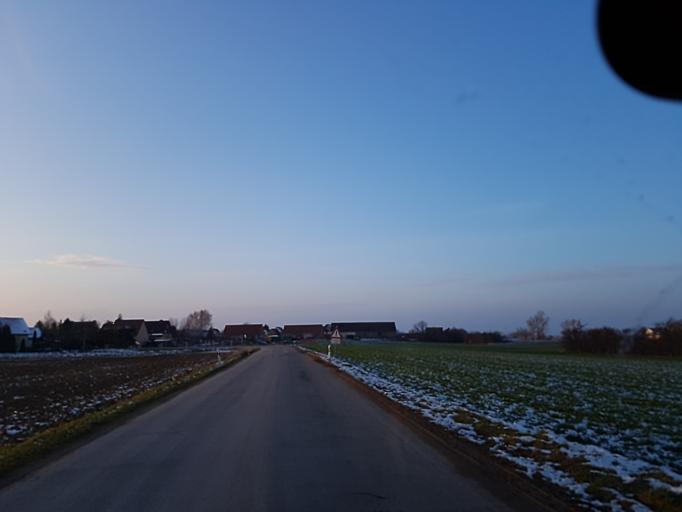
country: DE
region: Saxony
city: Strehla
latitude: 51.3863
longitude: 13.2076
